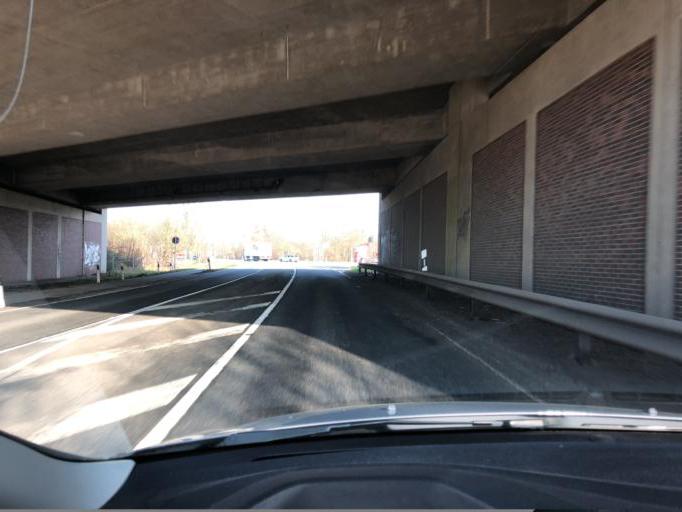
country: DE
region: Lower Saxony
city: Westerstede
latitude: 53.2799
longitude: 7.9013
